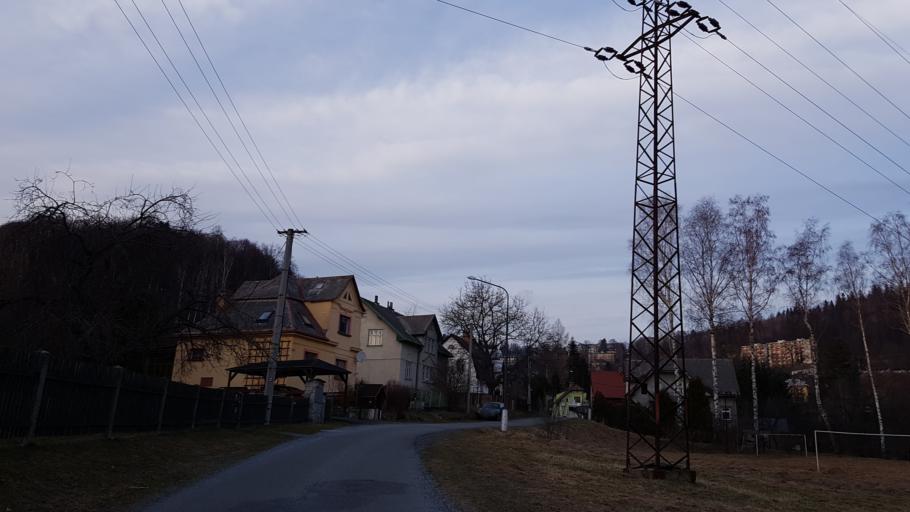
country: CZ
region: Olomoucky
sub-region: Okres Jesenik
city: Jesenik
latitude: 50.2311
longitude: 17.1851
